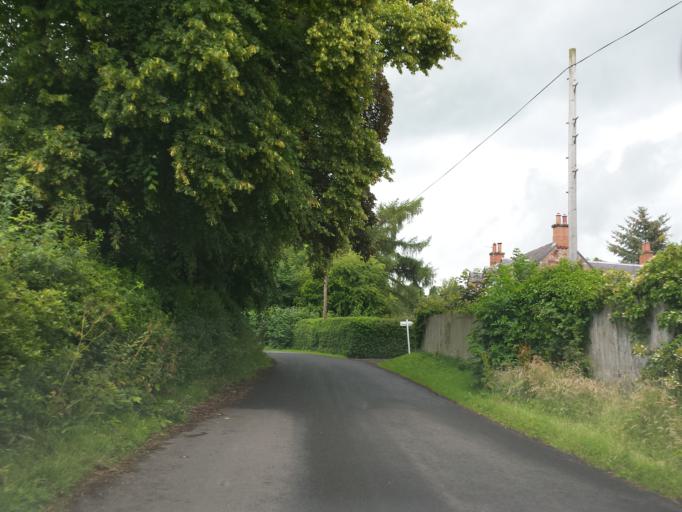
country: GB
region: Scotland
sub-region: The Scottish Borders
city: Saint Boswells
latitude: 55.5796
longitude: -2.6479
